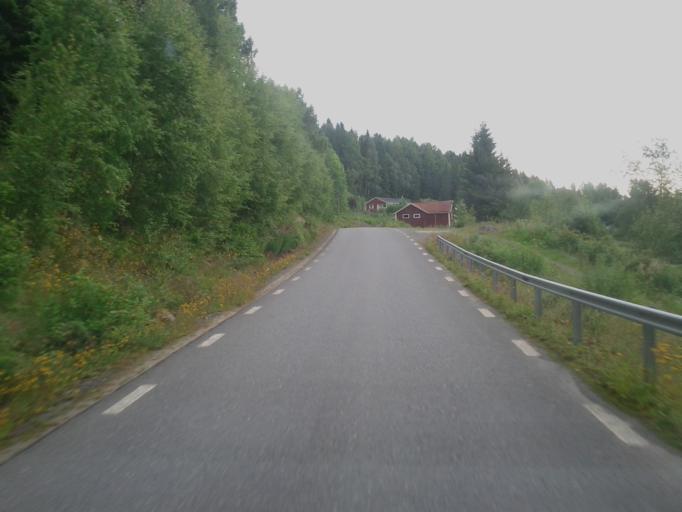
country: SE
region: Vaesternorrland
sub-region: Kramfors Kommun
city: Nordingra
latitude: 63.0622
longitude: 18.3894
